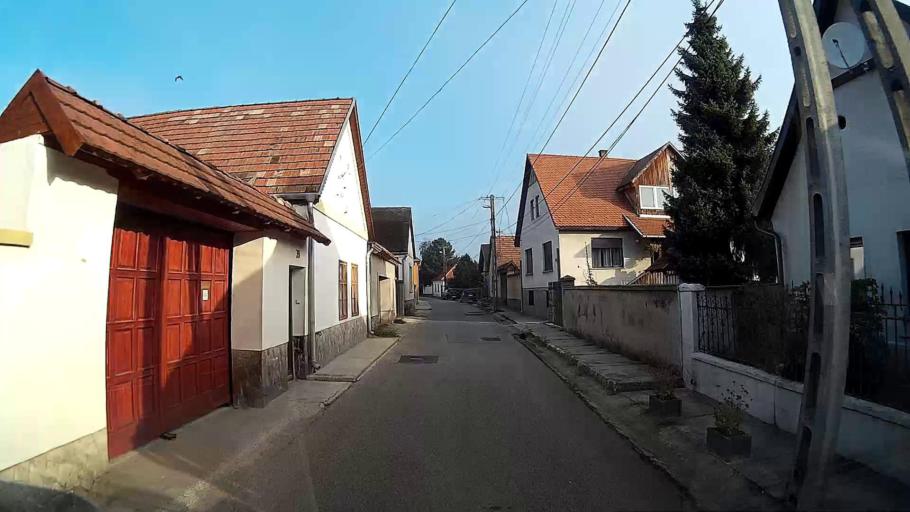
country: HU
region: Pest
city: Tahitotfalu
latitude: 47.7524
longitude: 19.0934
